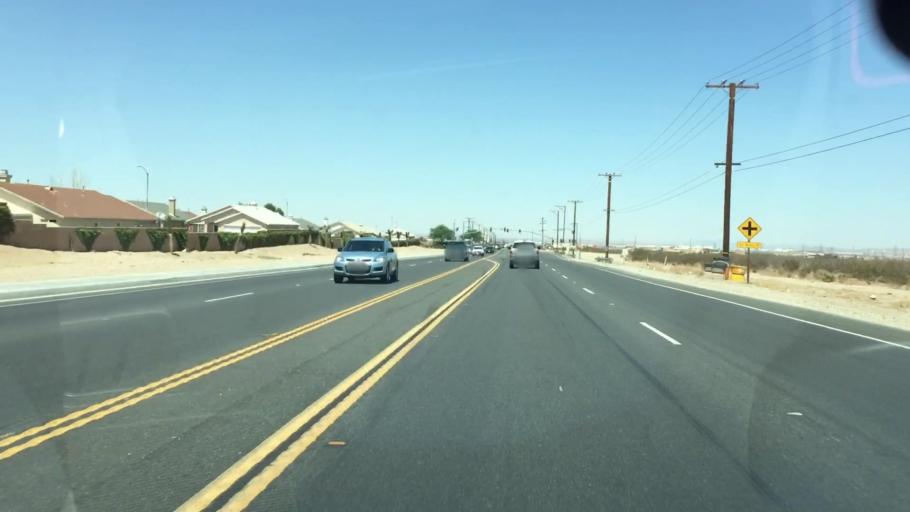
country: US
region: California
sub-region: San Bernardino County
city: Mountain View Acres
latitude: 34.4967
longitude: -117.3995
